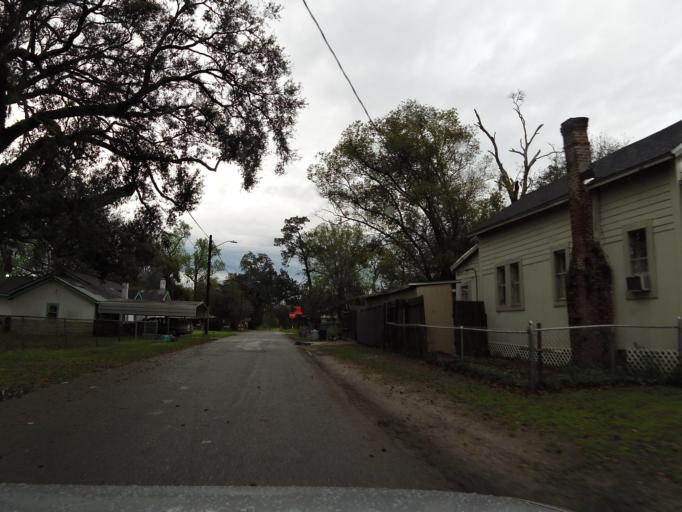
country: US
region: Florida
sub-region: Duval County
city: Jacksonville
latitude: 30.3247
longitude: -81.6996
